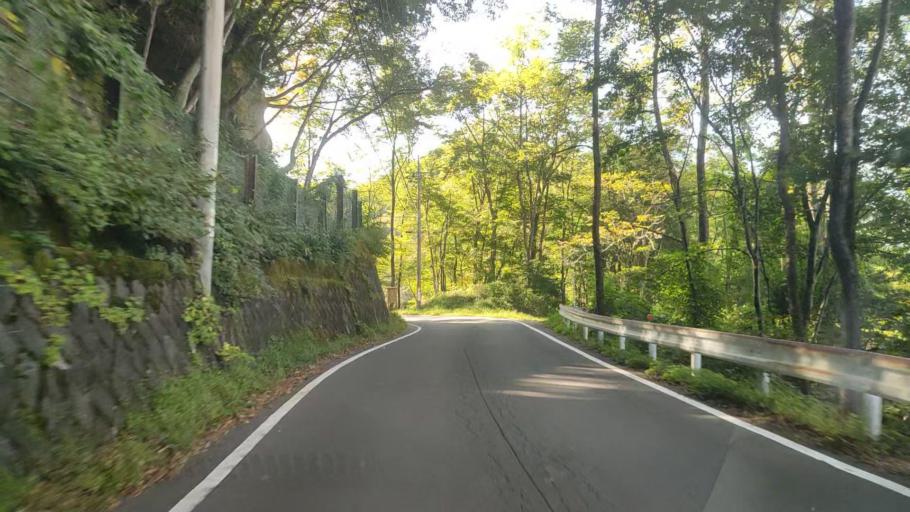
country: JP
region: Gunma
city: Nakanojomachi
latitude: 36.5993
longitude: 138.6401
